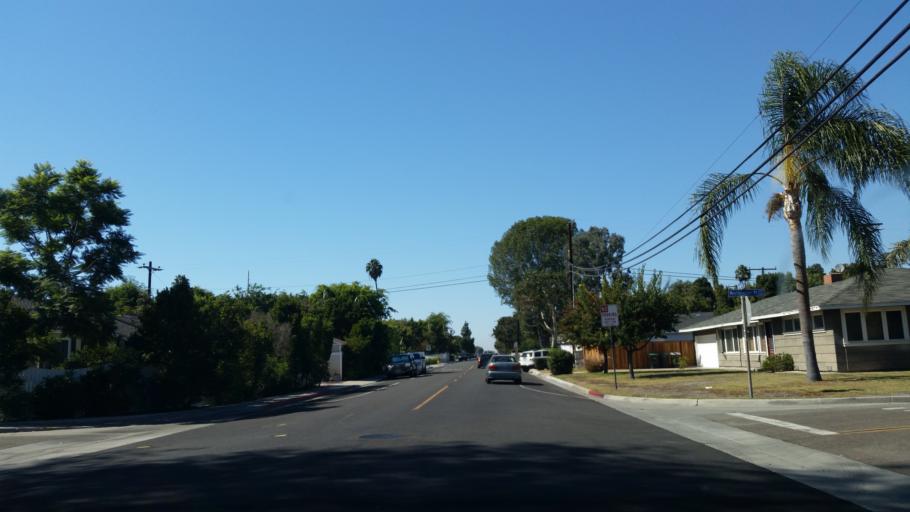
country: US
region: California
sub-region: Orange County
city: Costa Mesa
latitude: 33.6591
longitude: -117.8916
